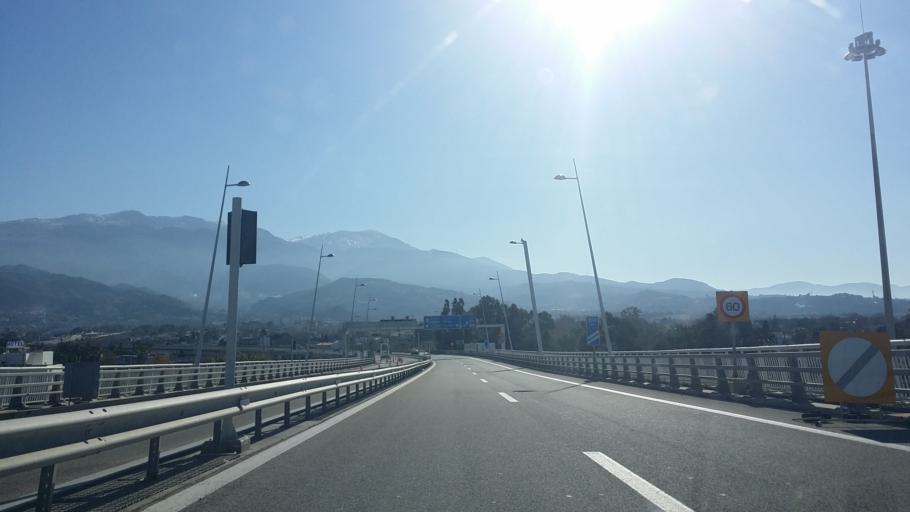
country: GR
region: West Greece
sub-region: Nomos Achaias
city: Rio
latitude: 38.3093
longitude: 21.7793
